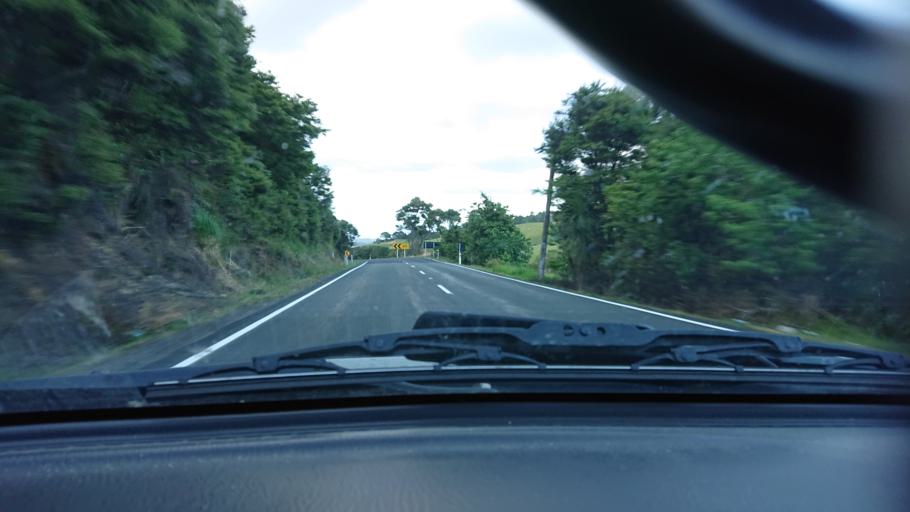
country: NZ
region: Auckland
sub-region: Auckland
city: Wellsford
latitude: -36.4588
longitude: 174.4439
